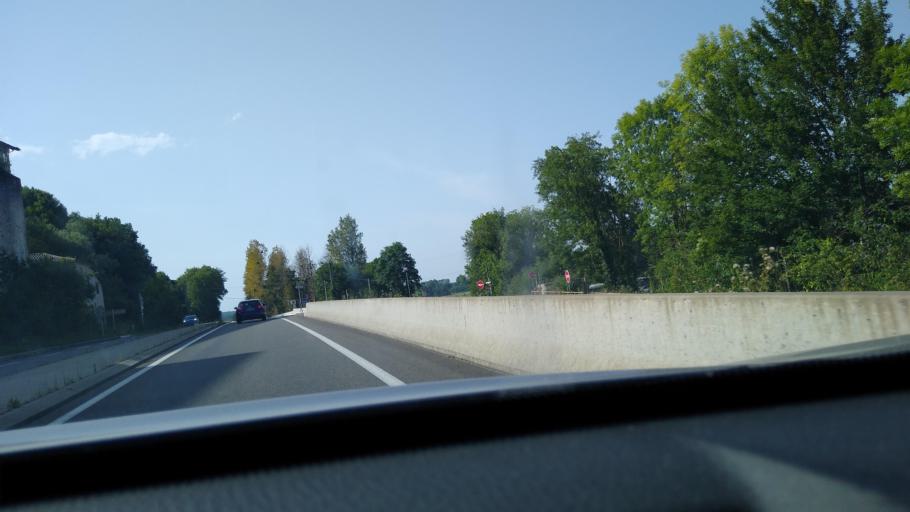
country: FR
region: Midi-Pyrenees
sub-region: Departement de la Haute-Garonne
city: Salies-du-Salat
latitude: 43.0390
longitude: 0.9945
